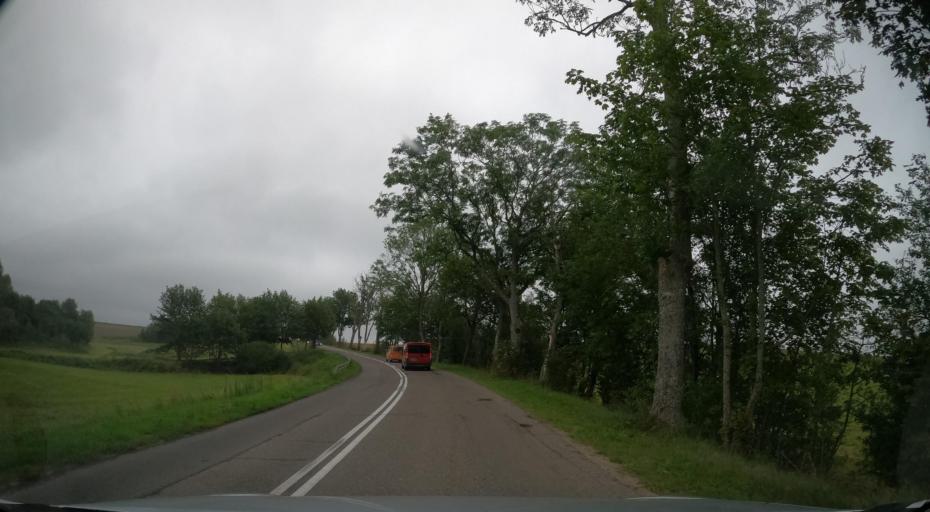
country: PL
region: Pomeranian Voivodeship
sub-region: Powiat wejherowski
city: Luzino
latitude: 54.4935
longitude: 18.1370
